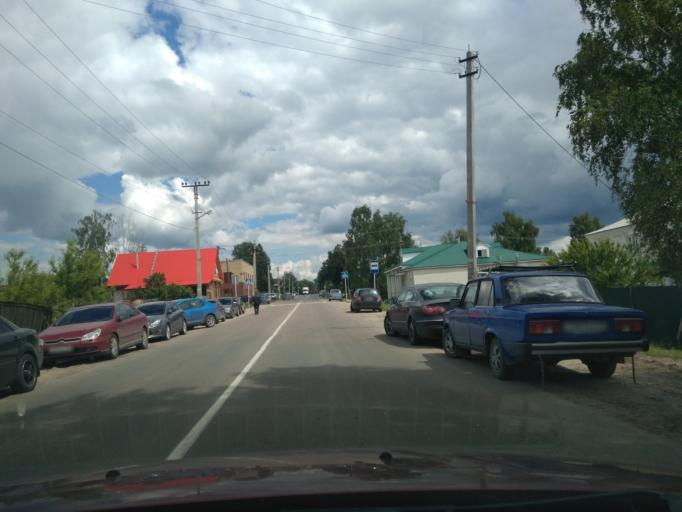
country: RU
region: Vladimir
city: Melenki
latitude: 55.3389
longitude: 41.6372
